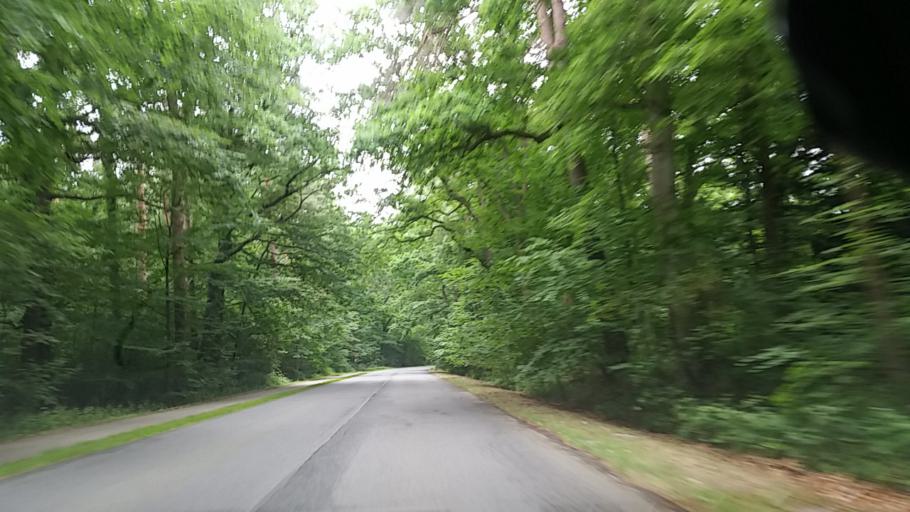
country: DE
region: Lower Saxony
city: Wolfsburg
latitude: 52.4581
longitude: 10.8047
